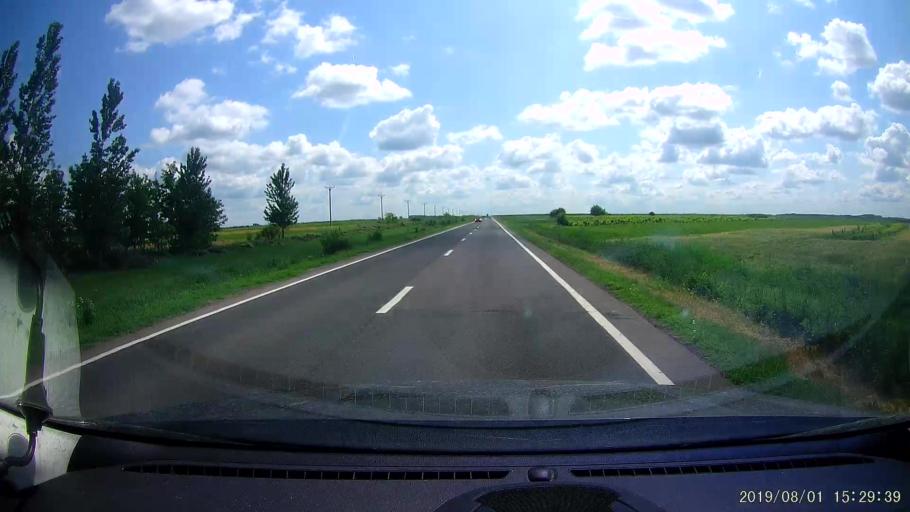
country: RO
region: Braila
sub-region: Comuna Viziru
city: Viziru
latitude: 44.9778
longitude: 27.6925
